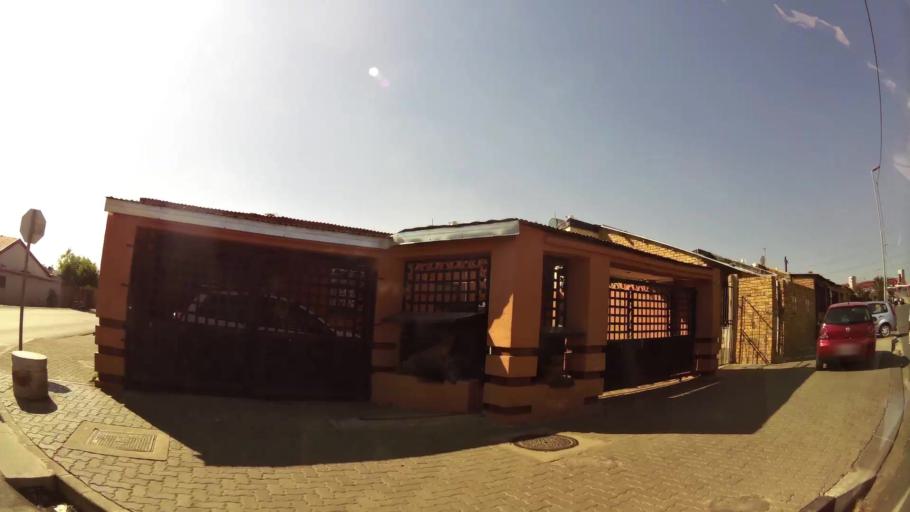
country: ZA
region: Gauteng
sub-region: City of Johannesburg Metropolitan Municipality
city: Johannesburg
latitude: -26.1857
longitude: 27.9751
